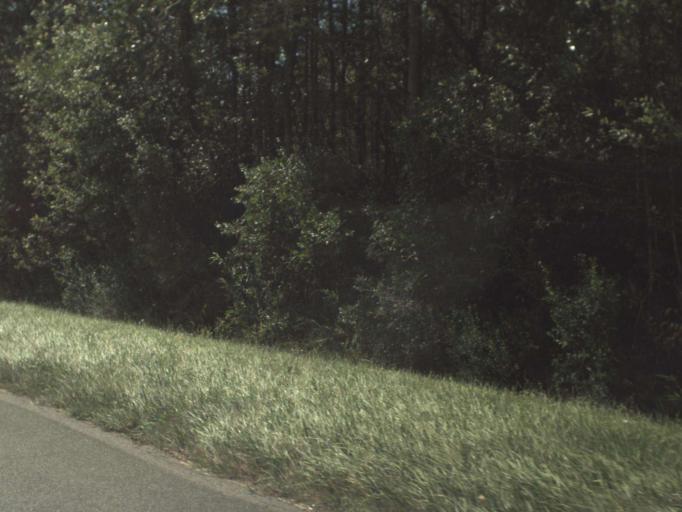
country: US
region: Florida
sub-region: Washington County
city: Chipley
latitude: 30.6453
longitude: -85.5841
